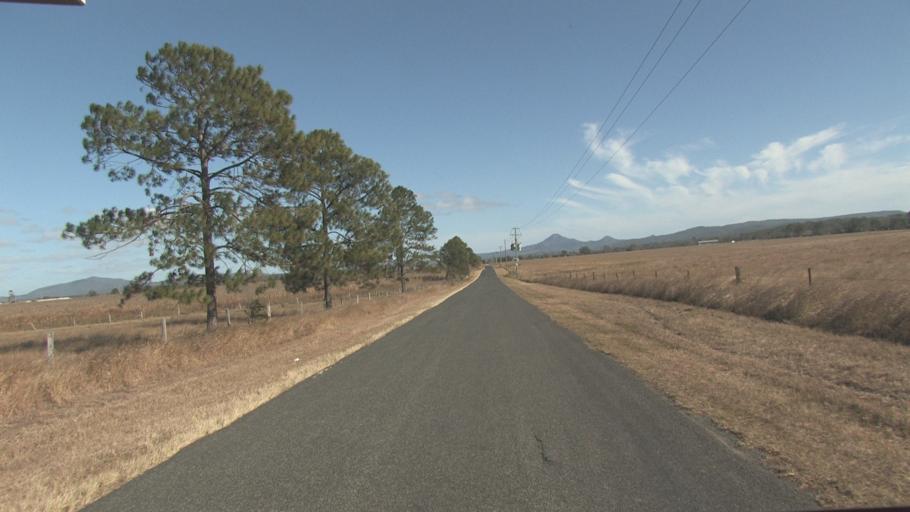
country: AU
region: Queensland
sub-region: Logan
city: Cedar Vale
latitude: -27.8537
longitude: 152.9659
